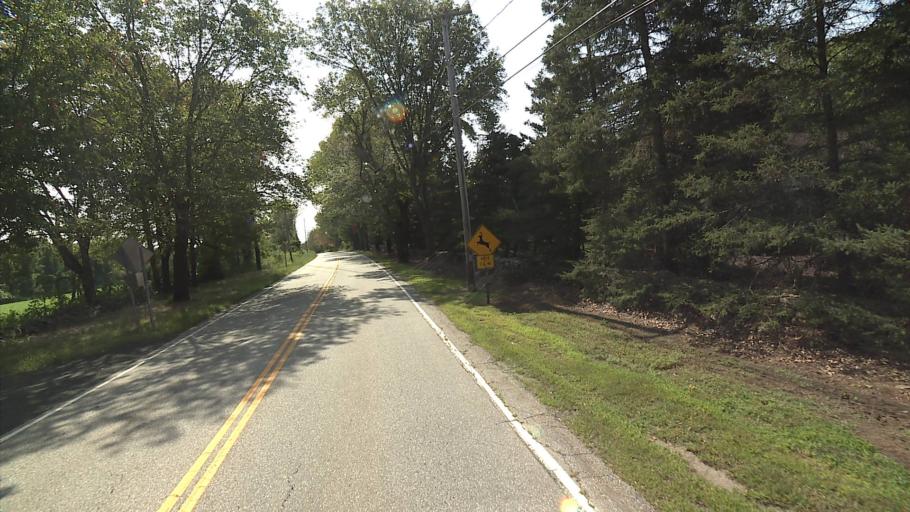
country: US
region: Connecticut
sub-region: Windham County
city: East Brooklyn
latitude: 41.8166
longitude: -71.9577
